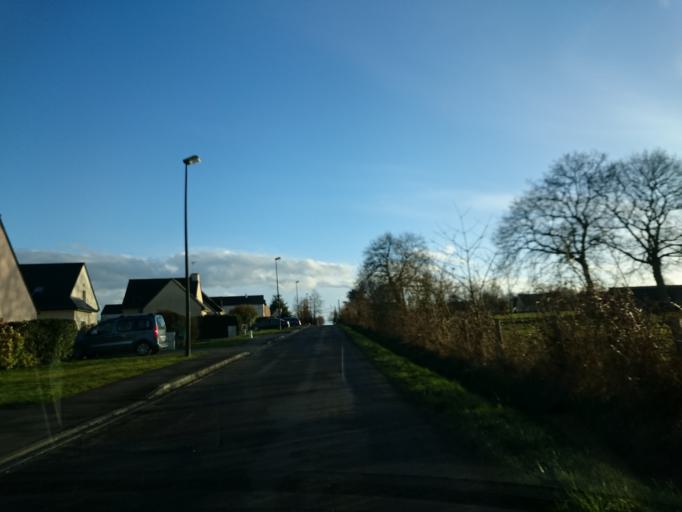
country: FR
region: Brittany
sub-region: Departement d'Ille-et-Vilaine
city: Crevin
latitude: 47.9411
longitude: -1.6537
